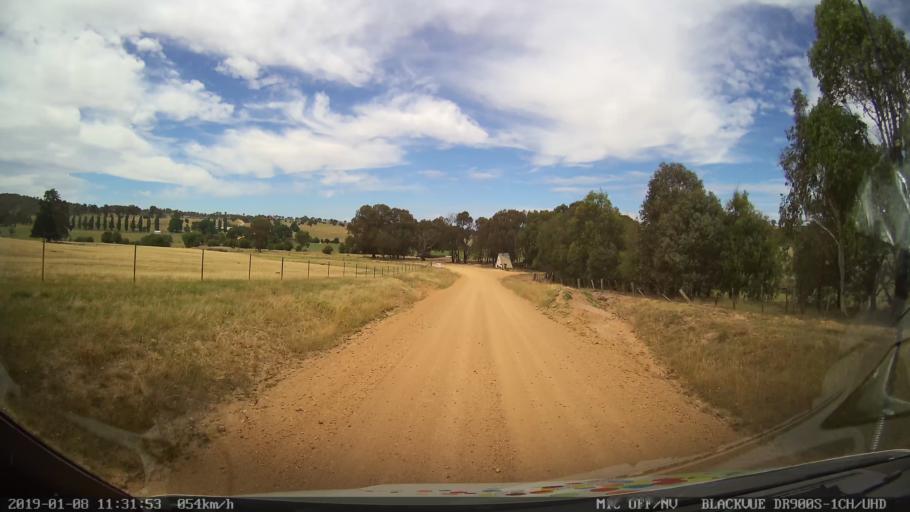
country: AU
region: New South Wales
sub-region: Guyra
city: Guyra
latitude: -30.3151
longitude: 151.5342
